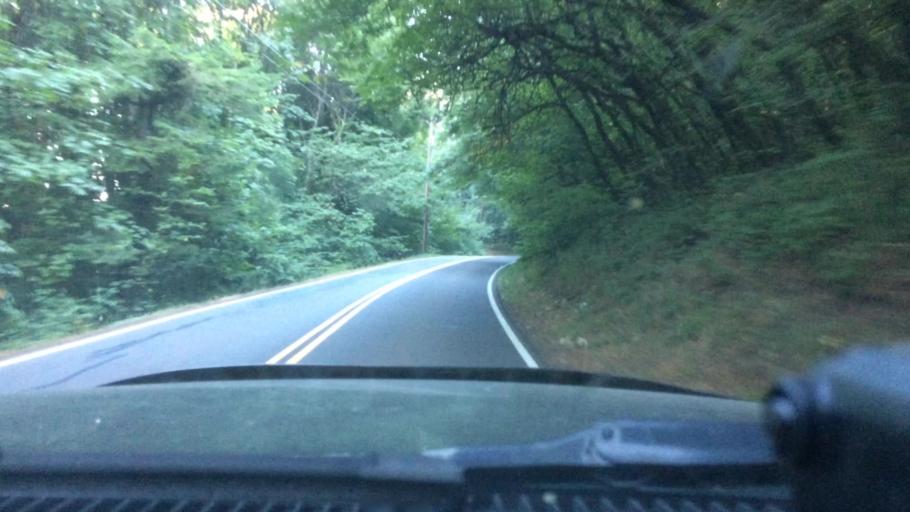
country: US
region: Oregon
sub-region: Yamhill County
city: Newberg
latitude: 45.3305
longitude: -122.9309
